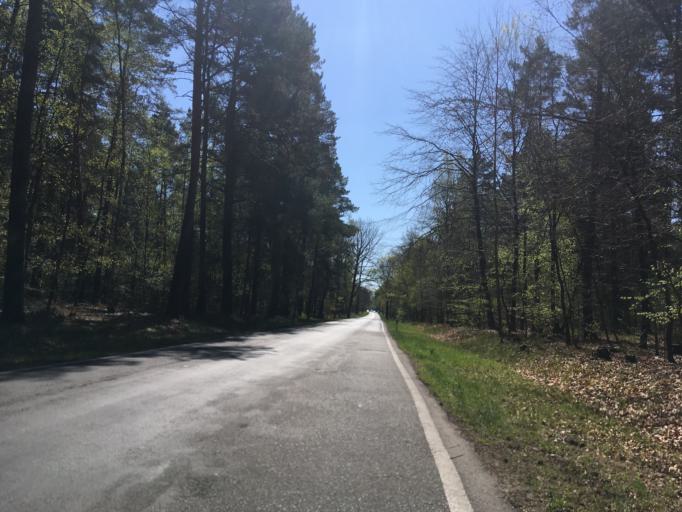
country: DE
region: Brandenburg
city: Bernau bei Berlin
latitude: 52.7127
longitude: 13.5794
